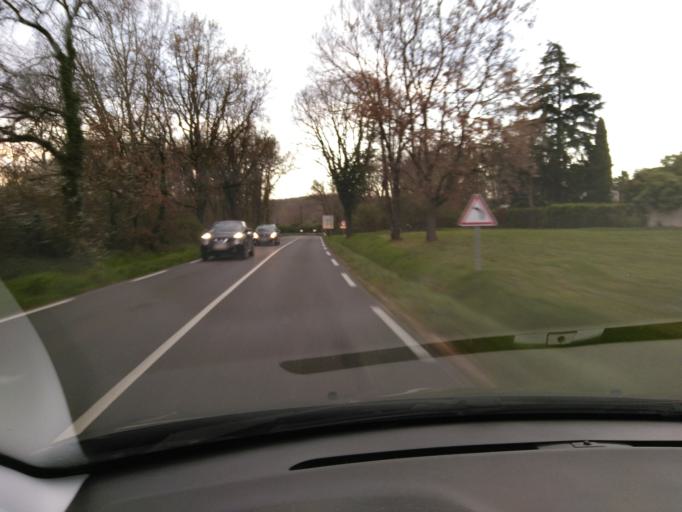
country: FR
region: Midi-Pyrenees
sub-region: Departement de la Haute-Garonne
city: Brax
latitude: 43.6141
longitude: 1.2606
